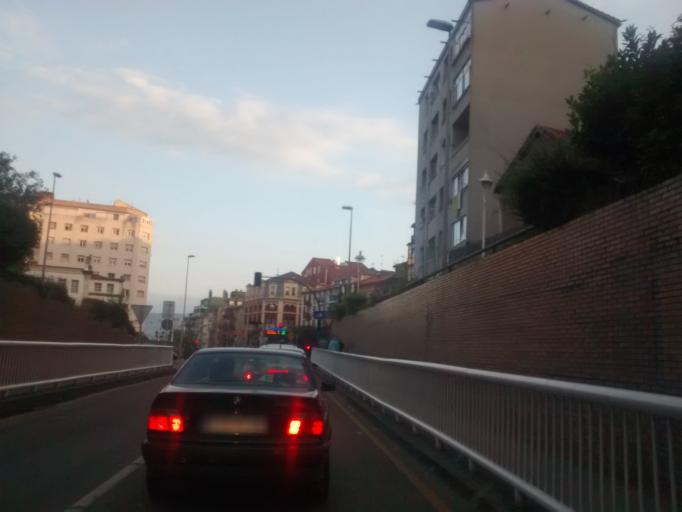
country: ES
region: Cantabria
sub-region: Provincia de Cantabria
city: Santander
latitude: 43.4658
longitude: -3.7968
